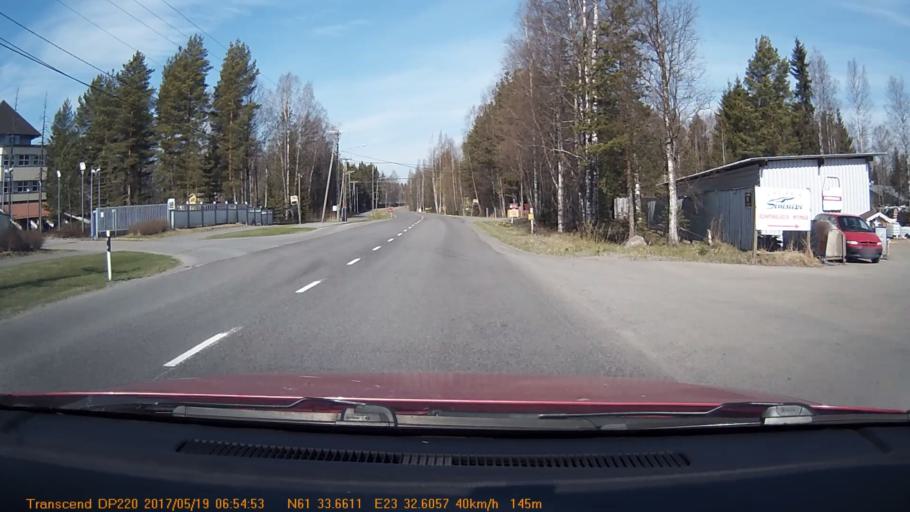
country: FI
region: Pirkanmaa
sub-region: Tampere
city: Yloejaervi
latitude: 61.5610
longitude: 23.5437
